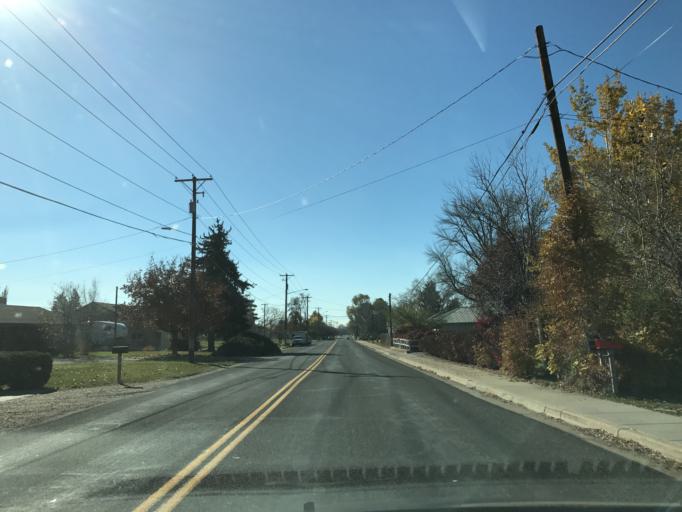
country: US
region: Utah
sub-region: Davis County
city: Layton
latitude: 41.0675
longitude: -111.9648
